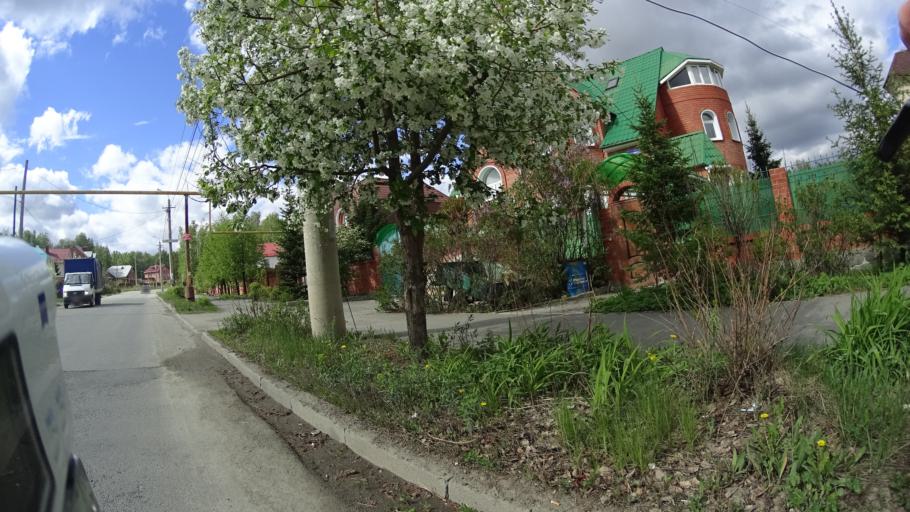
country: RU
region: Chelyabinsk
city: Sargazy
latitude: 55.1546
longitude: 61.2540
